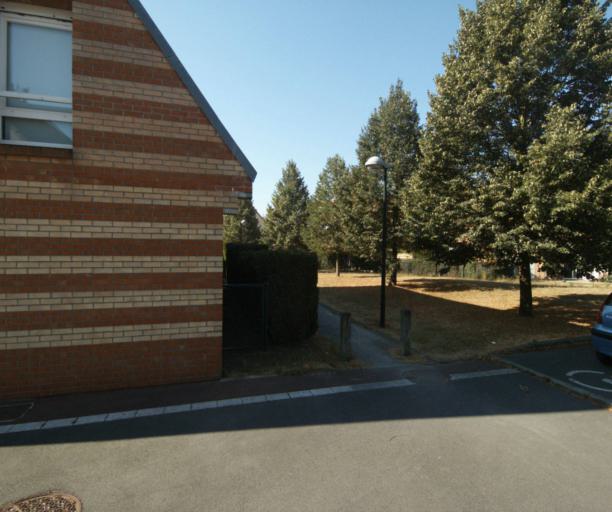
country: FR
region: Nord-Pas-de-Calais
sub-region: Departement du Nord
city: Wervicq-Sud
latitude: 50.7742
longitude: 3.0476
